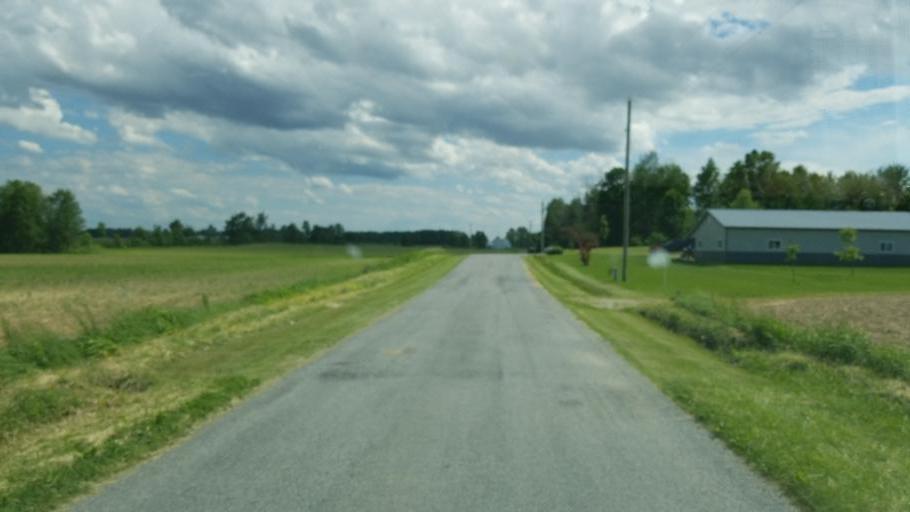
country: US
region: Ohio
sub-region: Huron County
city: Plymouth
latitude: 40.9901
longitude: -82.6182
